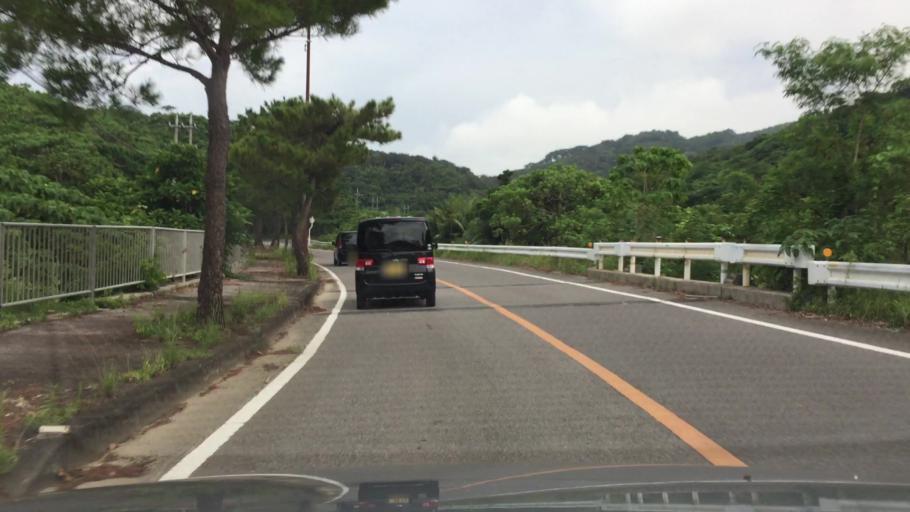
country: JP
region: Okinawa
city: Ishigaki
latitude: 24.3816
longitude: 124.1533
